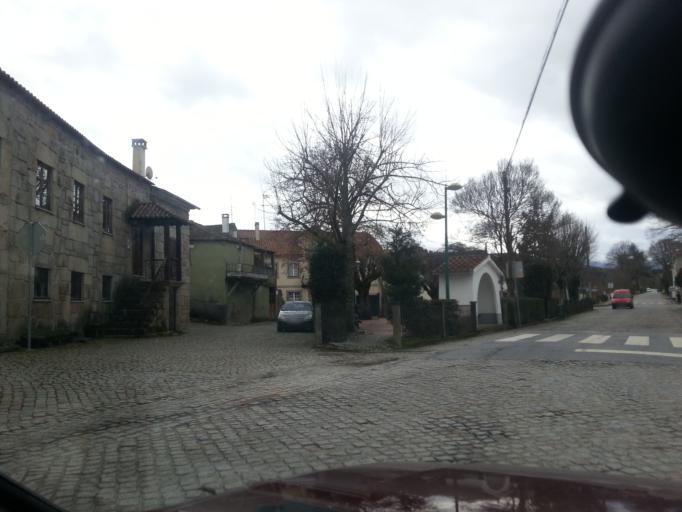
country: PT
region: Guarda
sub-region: Fornos de Algodres
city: Fornos de Algodres
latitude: 40.5876
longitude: -7.5392
